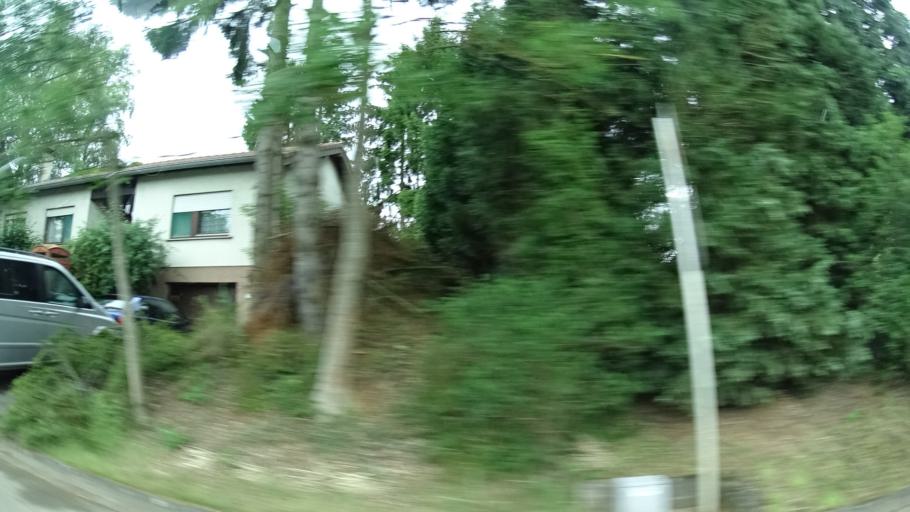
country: LU
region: Luxembourg
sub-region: Canton de Capellen
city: Garnich
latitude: 49.5989
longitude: 5.9474
